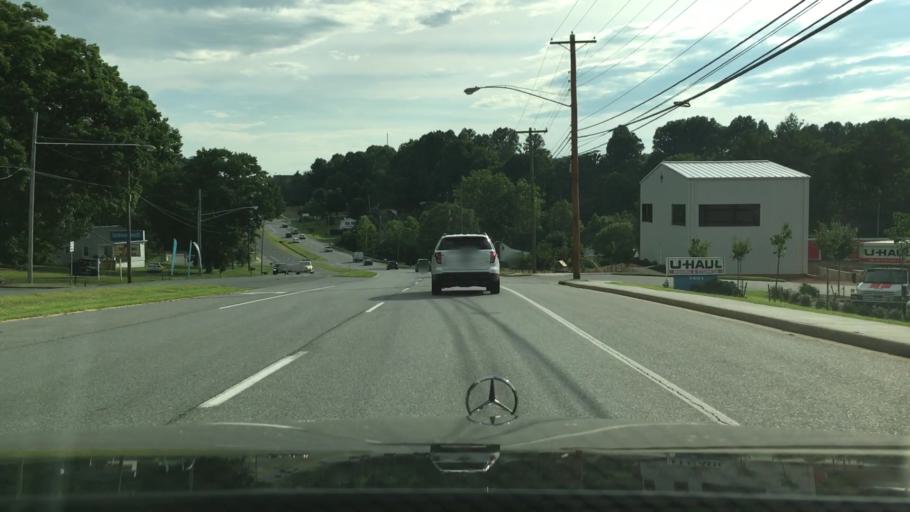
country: US
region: Virginia
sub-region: Campbell County
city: Timberlake
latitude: 37.3591
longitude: -79.2159
